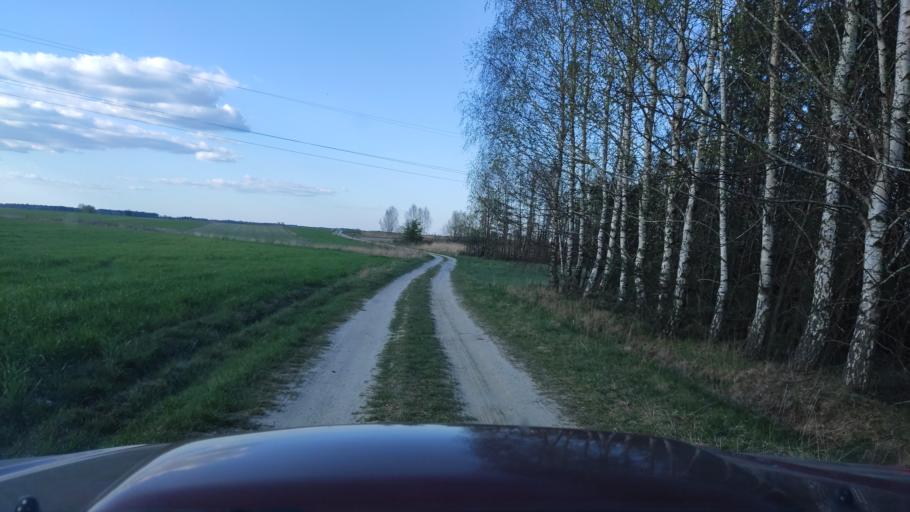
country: PL
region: Masovian Voivodeship
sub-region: Powiat zwolenski
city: Zwolen
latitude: 51.3708
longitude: 21.5749
